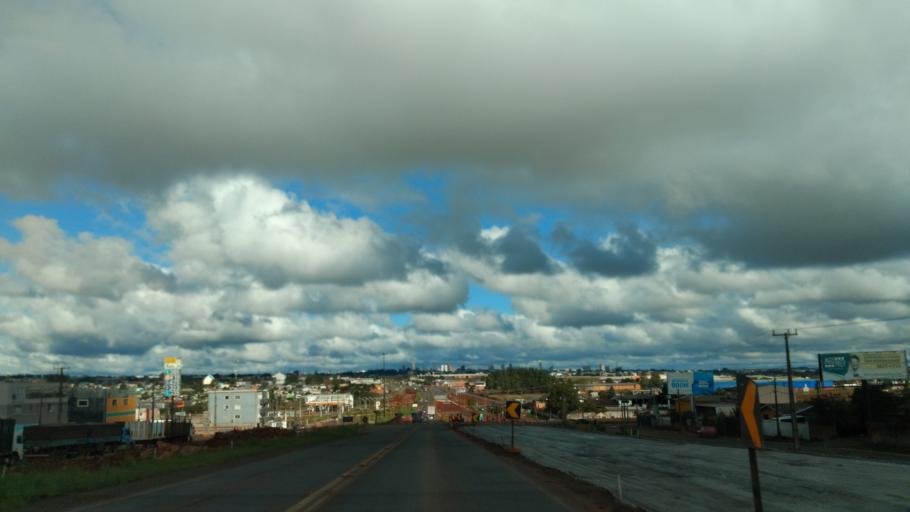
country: BR
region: Parana
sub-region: Guarapuava
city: Guarapuava
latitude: -25.3490
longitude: -51.4879
